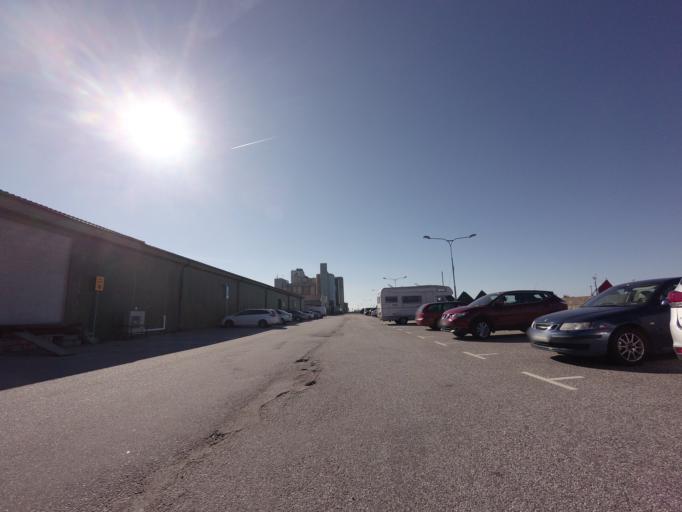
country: SE
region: Skane
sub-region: Ystads Kommun
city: Ystad
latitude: 55.4263
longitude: 13.8178
